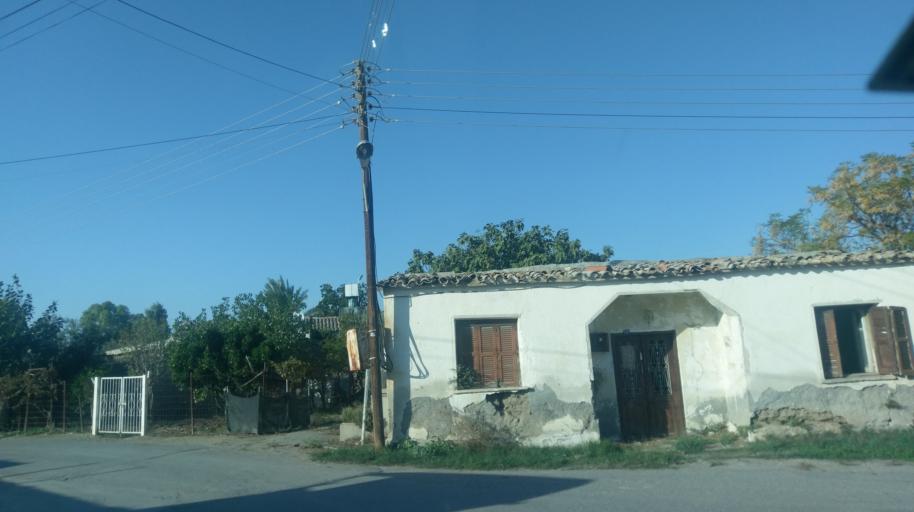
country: CY
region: Ammochostos
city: Lefkonoiko
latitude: 35.2539
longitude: 33.6873
